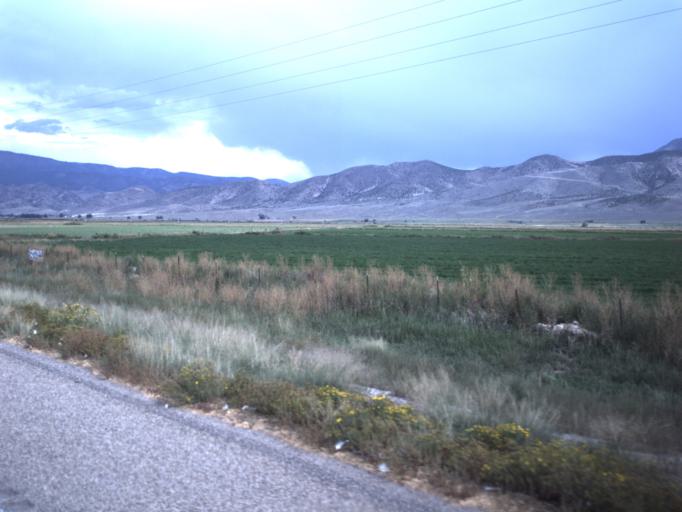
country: US
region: Utah
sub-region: Piute County
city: Junction
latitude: 38.1803
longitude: -112.2494
